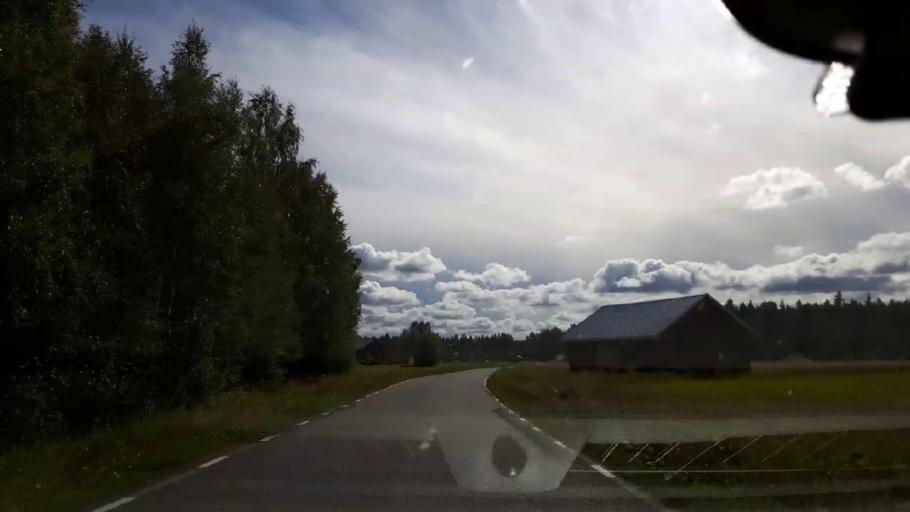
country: SE
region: Jaemtland
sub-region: Braecke Kommun
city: Braecke
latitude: 63.2098
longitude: 15.3501
